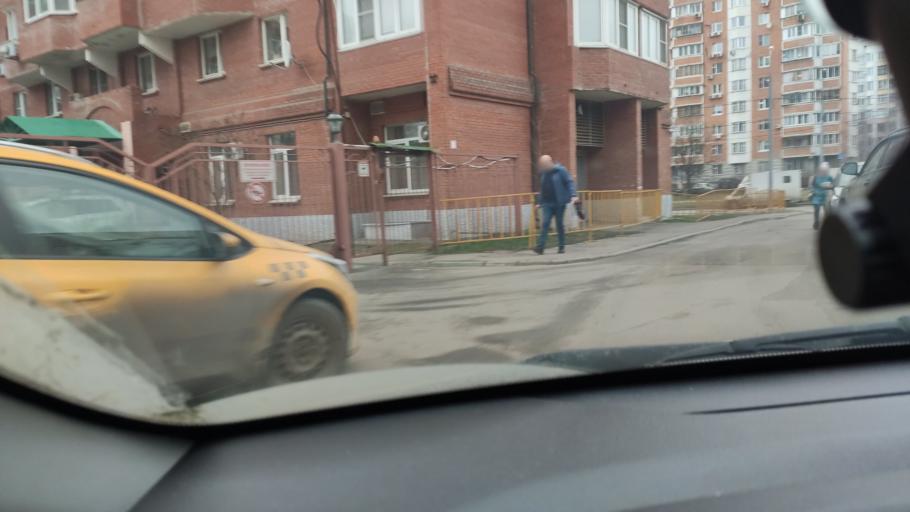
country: RU
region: Moskovskaya
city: Shcherbinka
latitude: 55.5365
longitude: 37.5310
